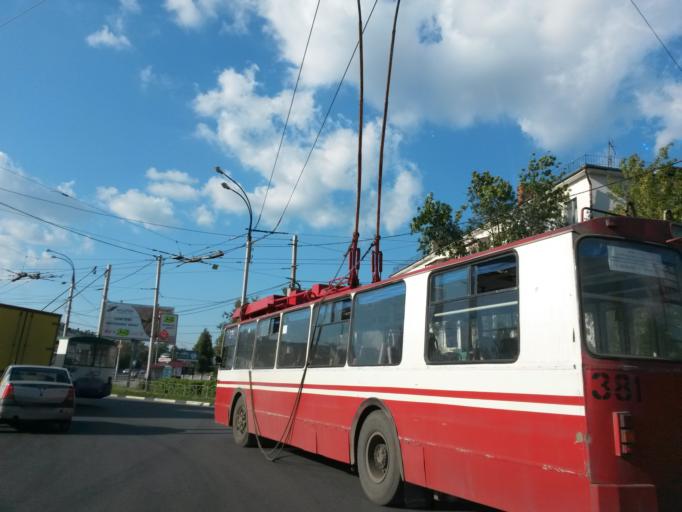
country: RU
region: Ivanovo
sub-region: Gorod Ivanovo
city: Ivanovo
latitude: 56.9645
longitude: 40.9739
